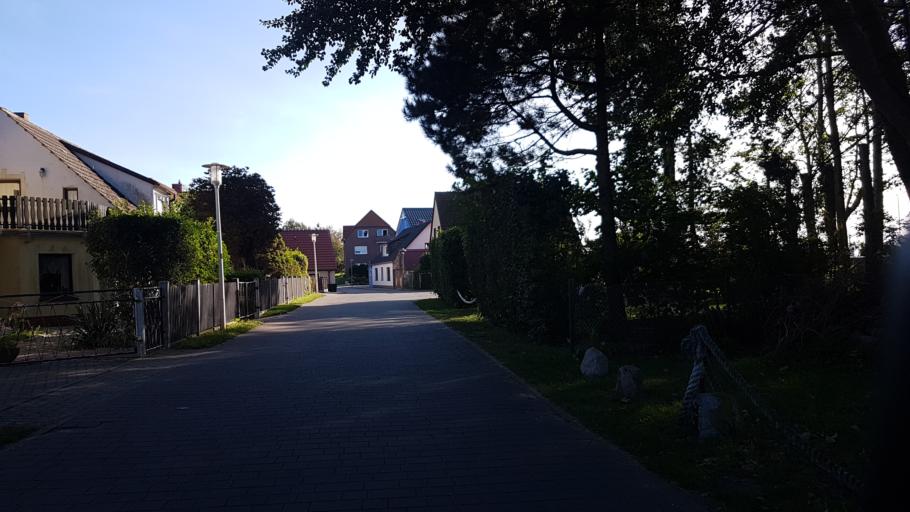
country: DE
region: Mecklenburg-Vorpommern
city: Wiek
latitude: 54.6232
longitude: 13.2871
